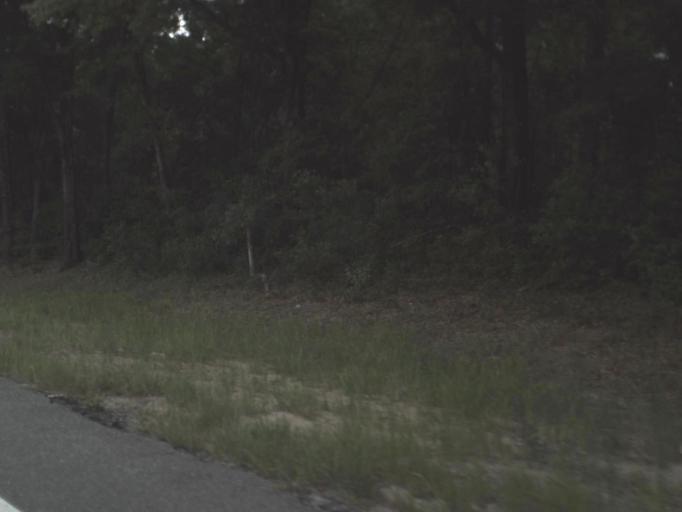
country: US
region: Florida
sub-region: Suwannee County
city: Wellborn
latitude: 30.3179
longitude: -82.7229
